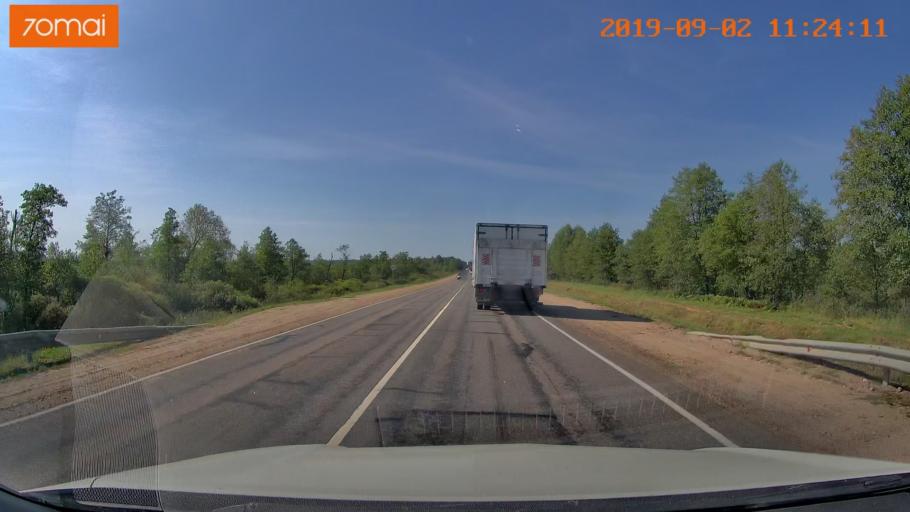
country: RU
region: Smolensk
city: Roslavl'
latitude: 54.0121
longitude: 32.9795
